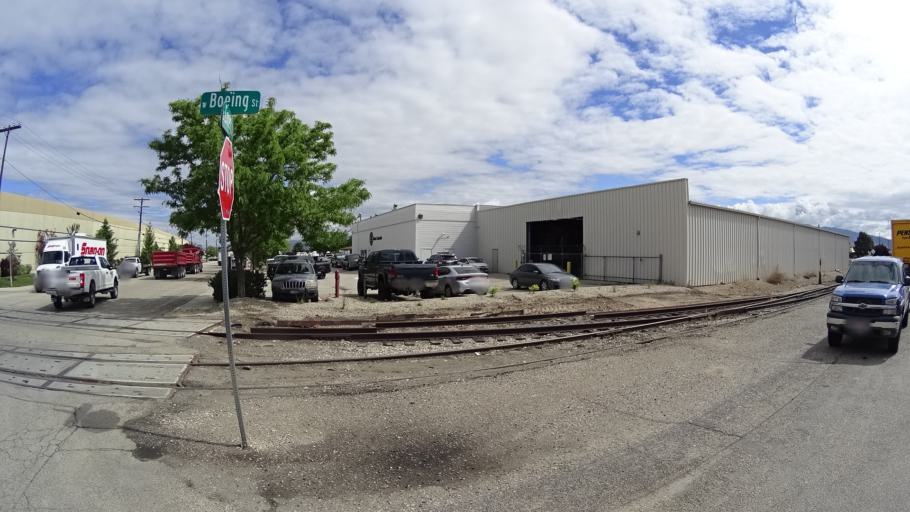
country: US
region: Idaho
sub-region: Ada County
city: Boise
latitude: 43.5625
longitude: -116.1986
